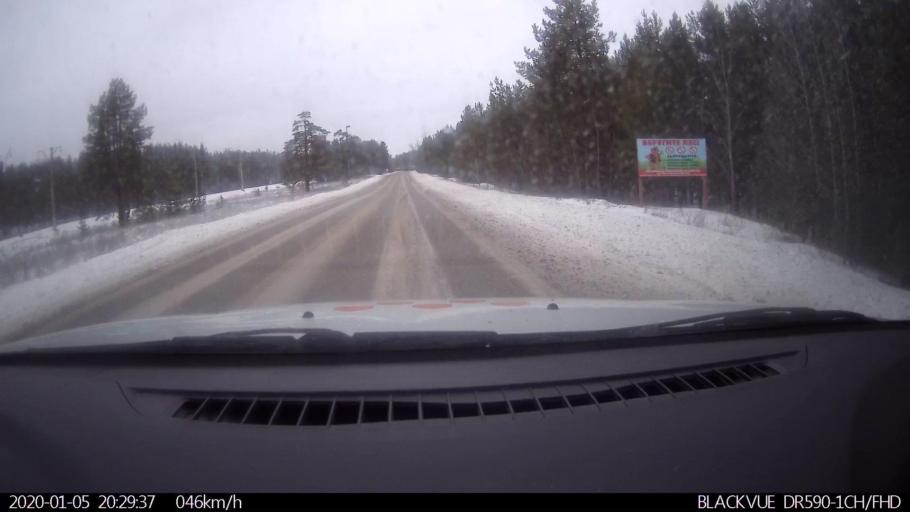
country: RU
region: Nizjnij Novgorod
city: Lukino
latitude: 56.3946
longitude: 43.7333
